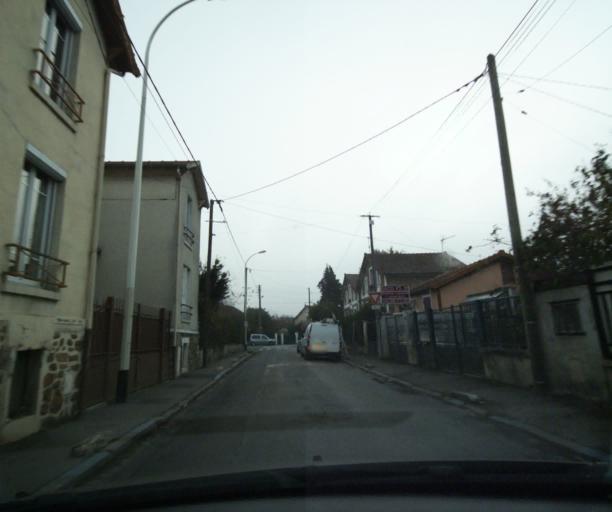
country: FR
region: Ile-de-France
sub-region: Departement de Seine-Saint-Denis
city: Neuilly-Plaisance
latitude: 48.8567
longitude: 2.5097
